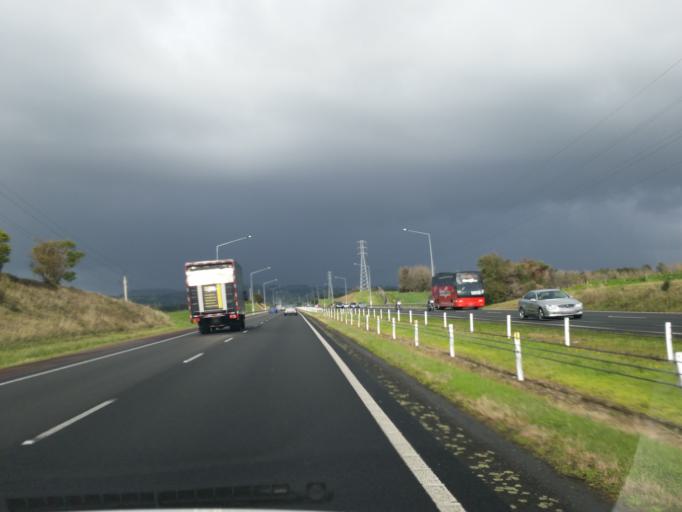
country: NZ
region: Auckland
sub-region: Auckland
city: Papakura
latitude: -37.1303
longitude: 174.9618
